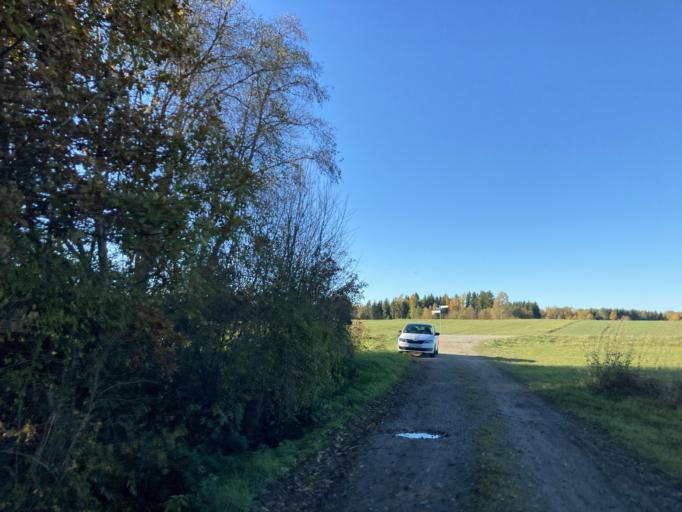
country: DE
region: Baden-Wuerttemberg
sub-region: Tuebingen Region
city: Ofterdingen
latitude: 48.4076
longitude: 9.0028
